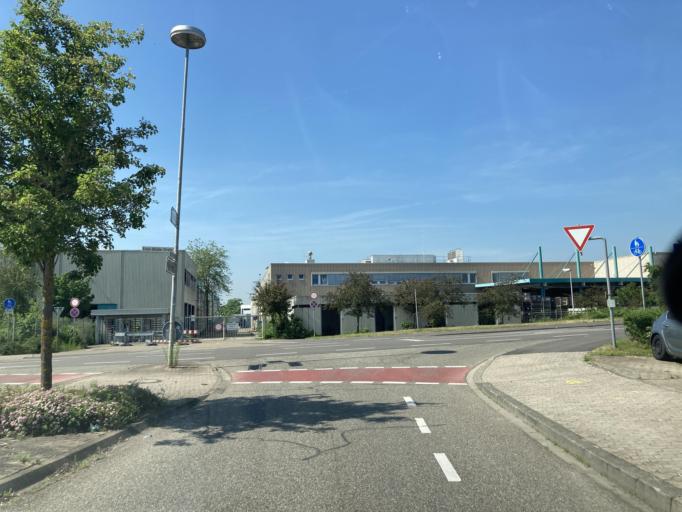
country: DE
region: Baden-Wuerttemberg
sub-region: Karlsruhe Region
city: Graben-Neudorf
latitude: 49.1588
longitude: 8.4930
